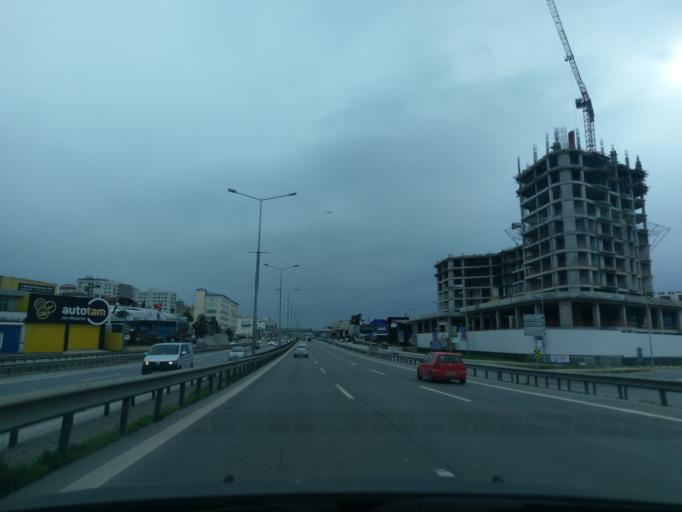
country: TR
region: Istanbul
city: Pendik
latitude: 40.8945
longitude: 29.2291
